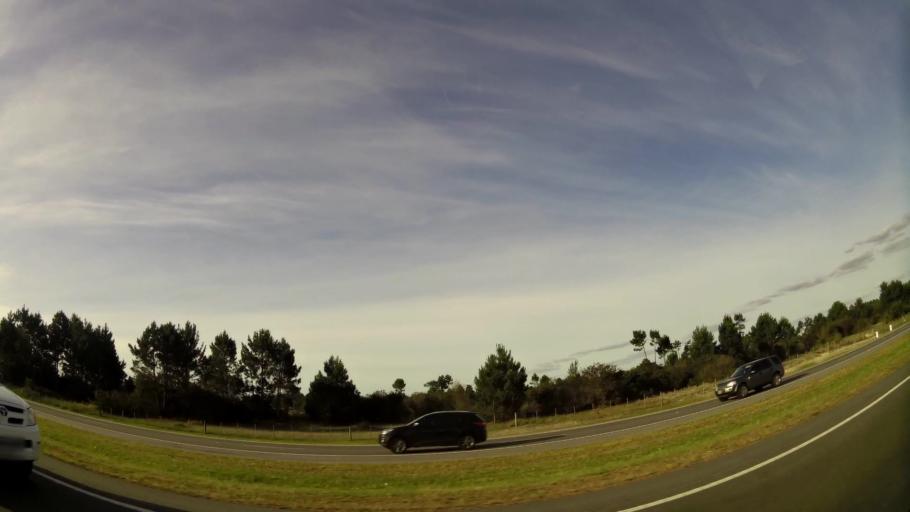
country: UY
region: Lavalleja
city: Solis de Mataojo
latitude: -34.7792
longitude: -55.4372
